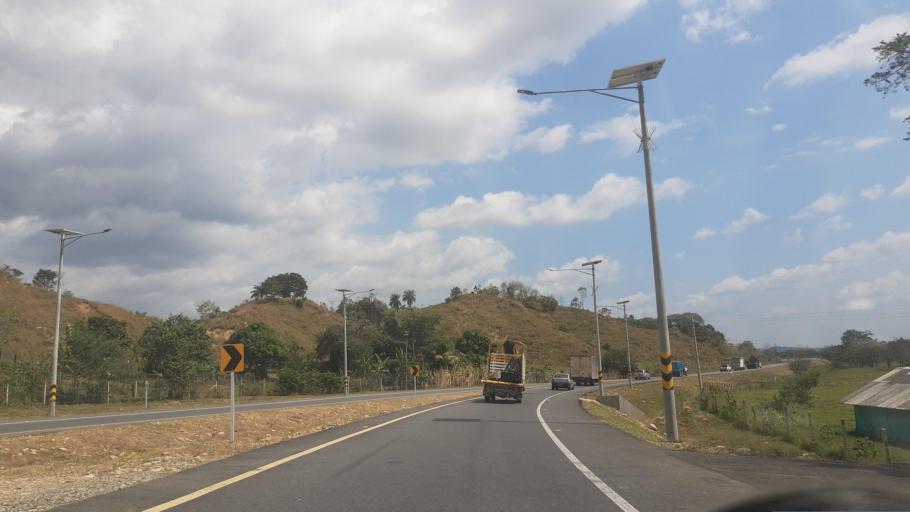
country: CO
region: Casanare
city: Tauramena
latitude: 5.0180
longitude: -72.6712
